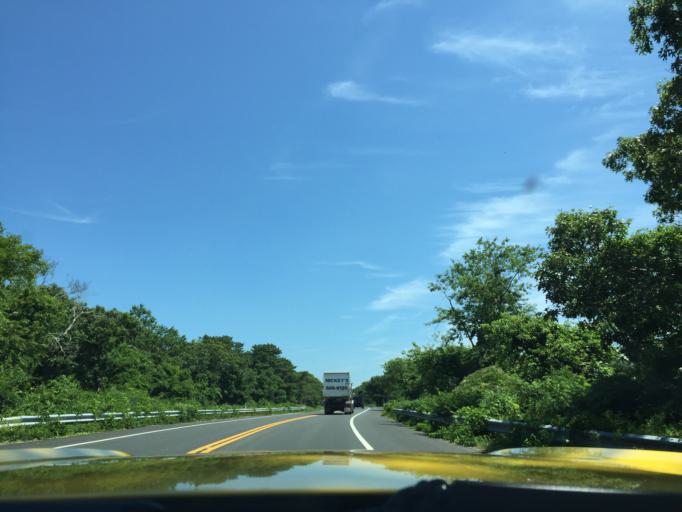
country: US
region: New York
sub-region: Suffolk County
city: Montauk
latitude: 41.0073
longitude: -72.0192
